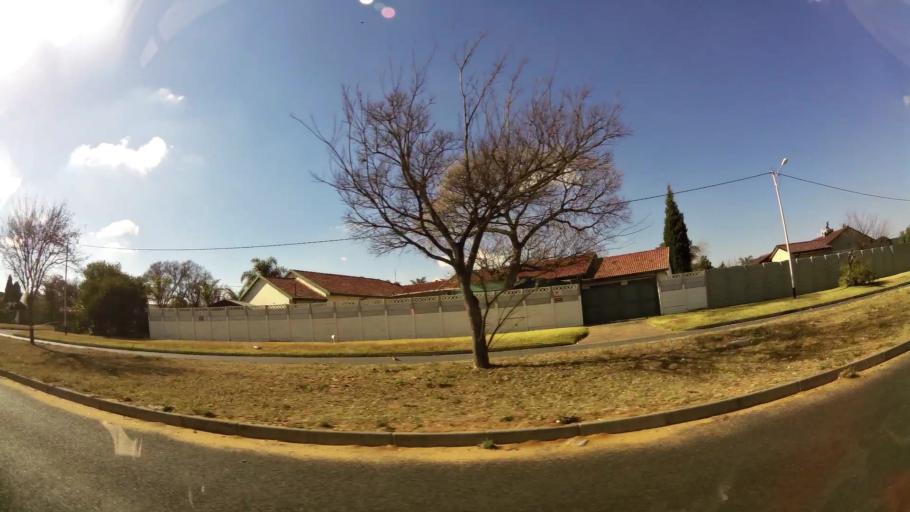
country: ZA
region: Gauteng
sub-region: City of Johannesburg Metropolitan Municipality
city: Roodepoort
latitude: -26.1423
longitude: 27.8266
